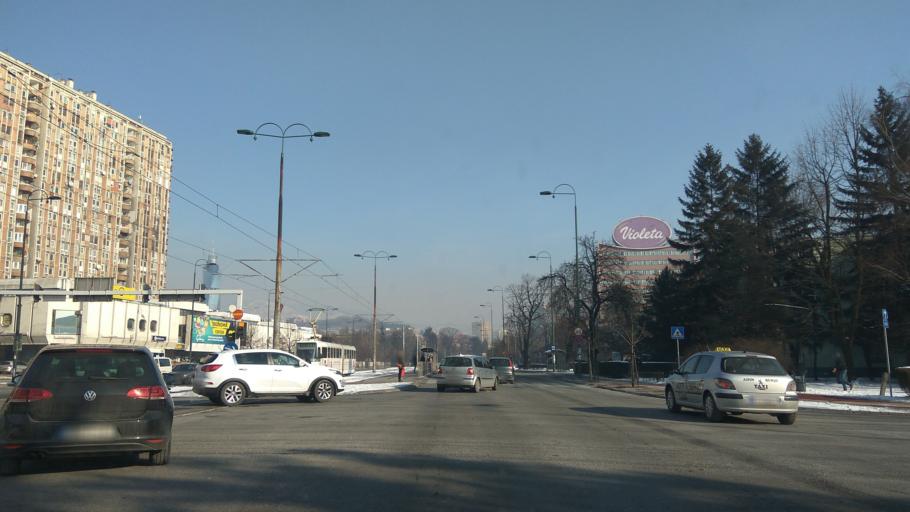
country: BA
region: Federation of Bosnia and Herzegovina
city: Kobilja Glava
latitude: 43.8540
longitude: 18.3924
